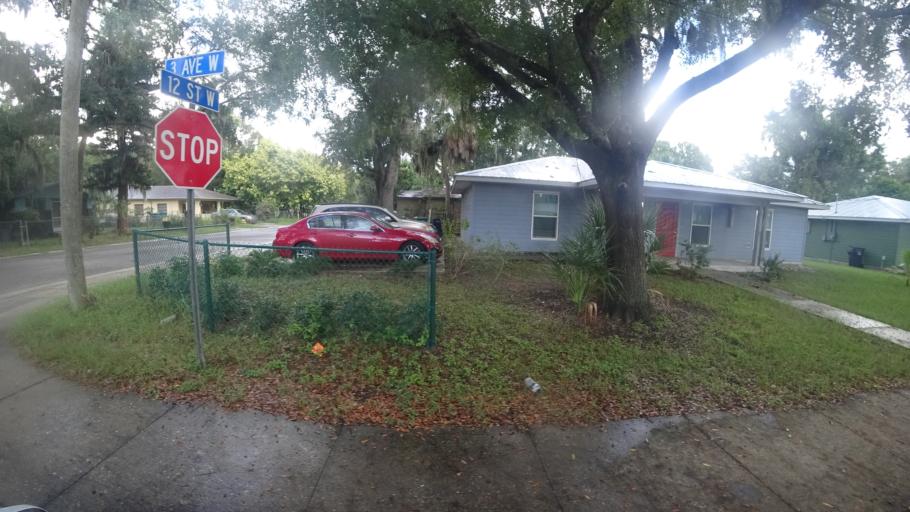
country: US
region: Florida
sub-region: Manatee County
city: Palmetto
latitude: 27.5238
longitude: -82.5662
